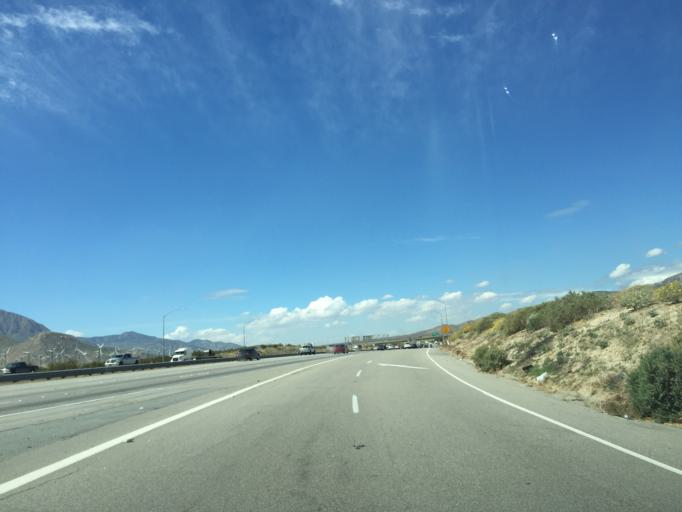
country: US
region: California
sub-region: Riverside County
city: Cabazon
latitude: 33.9230
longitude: -116.6835
